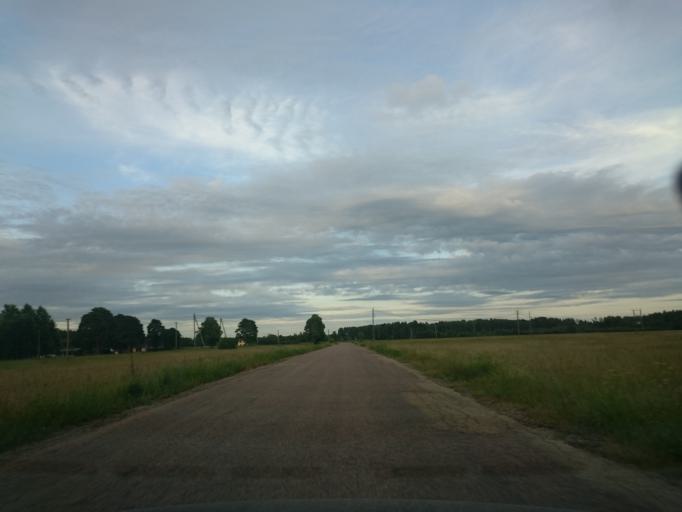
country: LV
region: Ropazu
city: Ropazi
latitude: 56.9692
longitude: 24.6561
